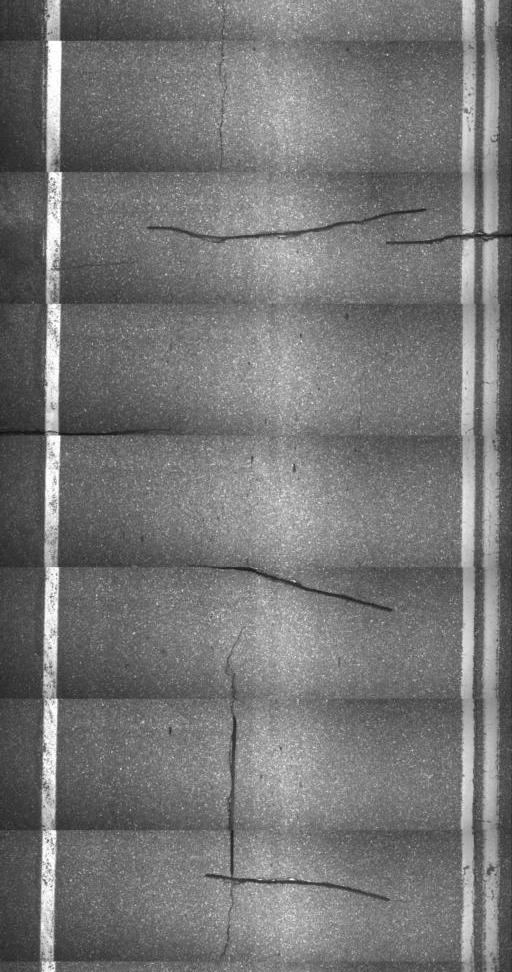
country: US
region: Vermont
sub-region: Caledonia County
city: Hardwick
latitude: 44.4141
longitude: -72.2169
